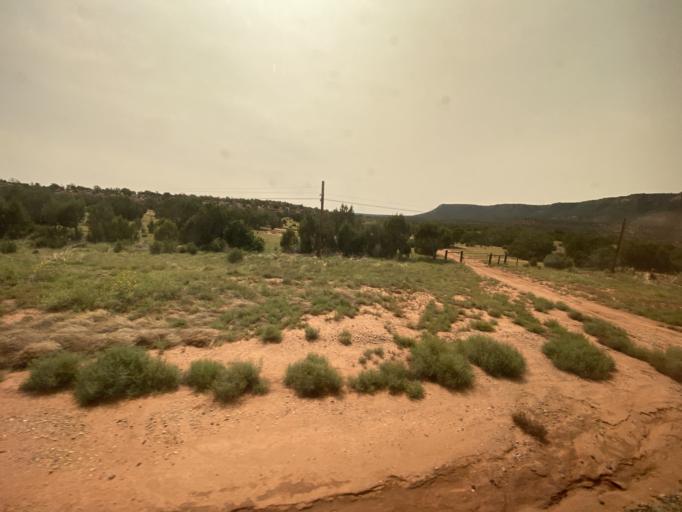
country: US
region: New Mexico
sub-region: San Miguel County
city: Pecos
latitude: 35.3918
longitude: -105.4813
